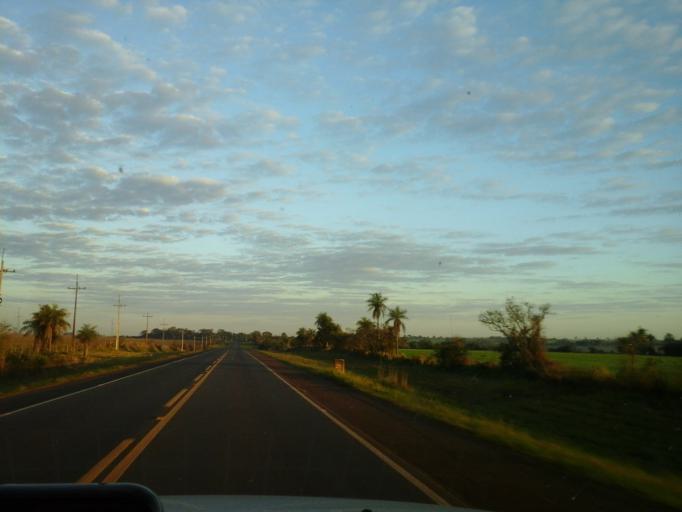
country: PY
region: Misiones
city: San Patricio
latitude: -27.0268
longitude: -56.6998
